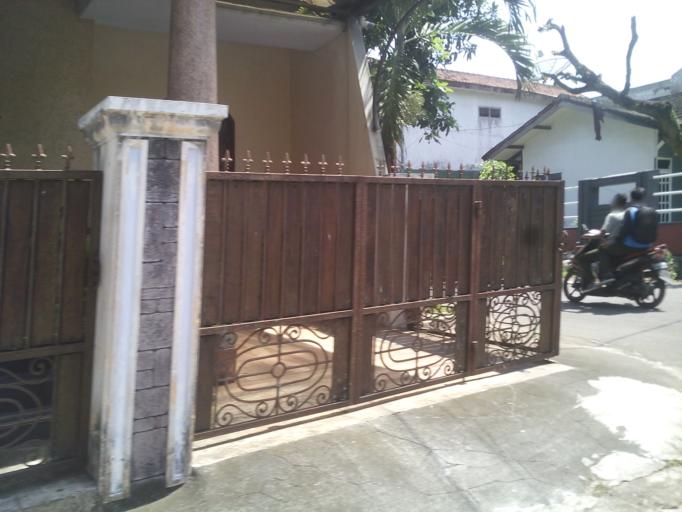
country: ID
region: East Java
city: Sumbersari Wetan
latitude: -8.1774
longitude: 113.7197
